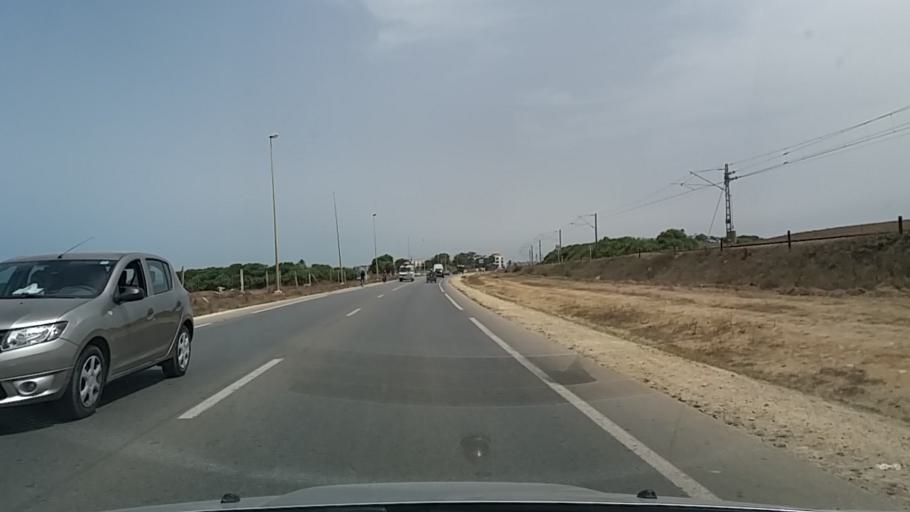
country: MA
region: Tanger-Tetouan
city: Asilah
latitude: 35.4913
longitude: -6.0199
